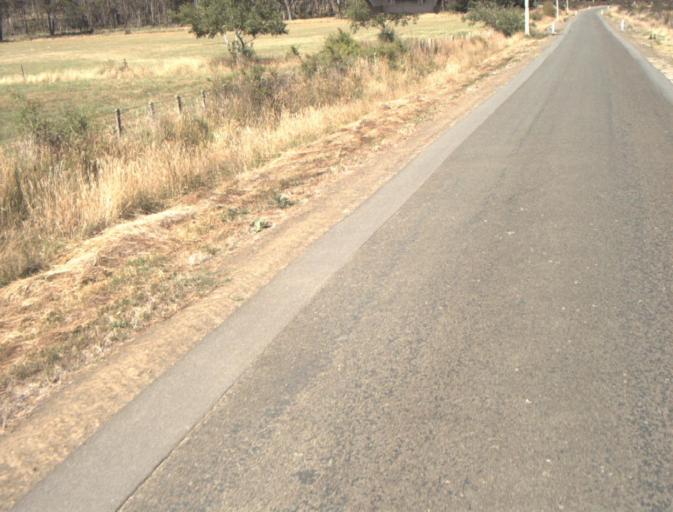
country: AU
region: Tasmania
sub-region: Launceston
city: Newstead
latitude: -41.3233
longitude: 147.3203
